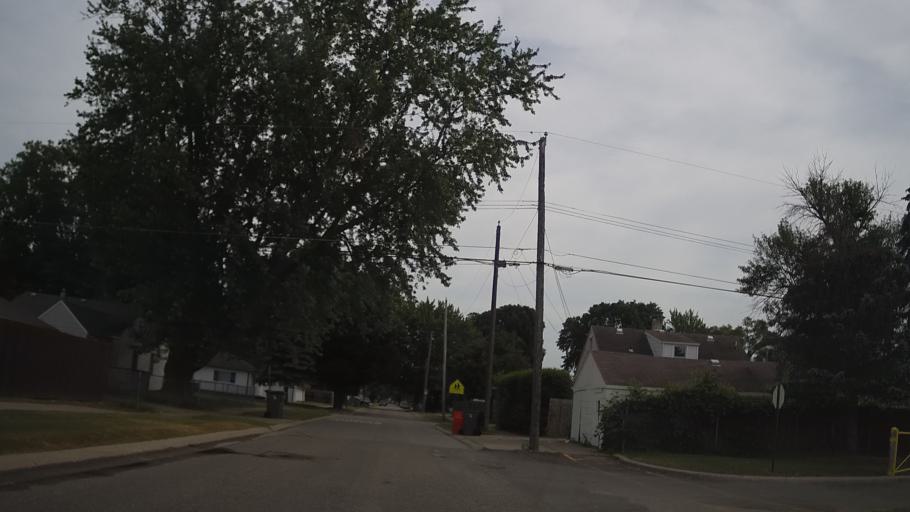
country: US
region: Michigan
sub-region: Macomb County
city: Fraser
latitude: 42.5449
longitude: -82.9135
